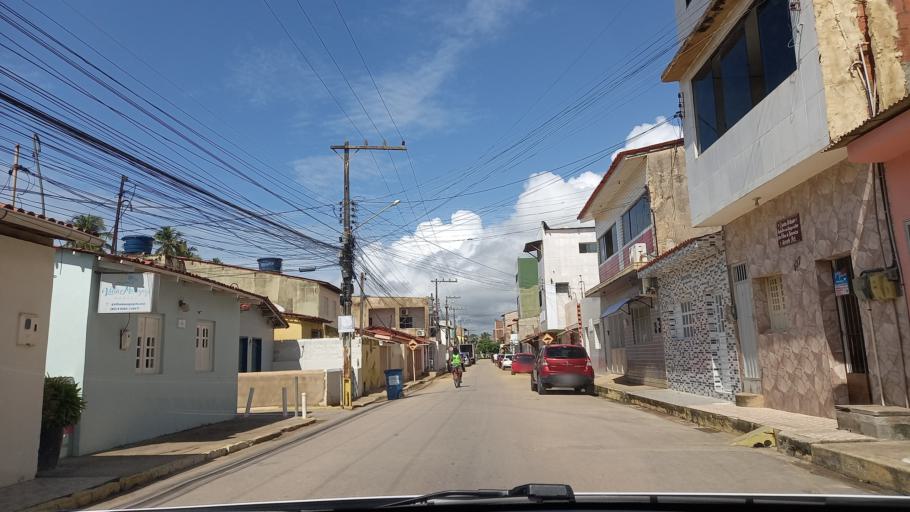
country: BR
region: Alagoas
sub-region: Maragogi
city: Maragogi
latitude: -9.0097
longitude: -35.2191
